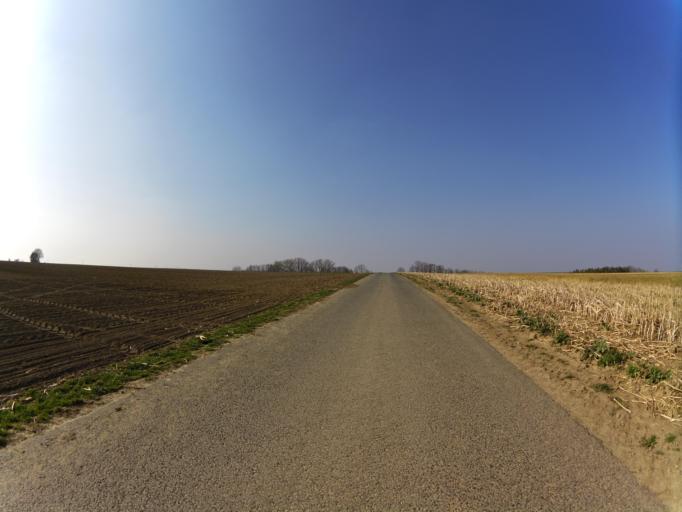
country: DE
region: Bavaria
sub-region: Regierungsbezirk Unterfranken
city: Gaukonigshofen
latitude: 49.6618
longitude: 9.9926
